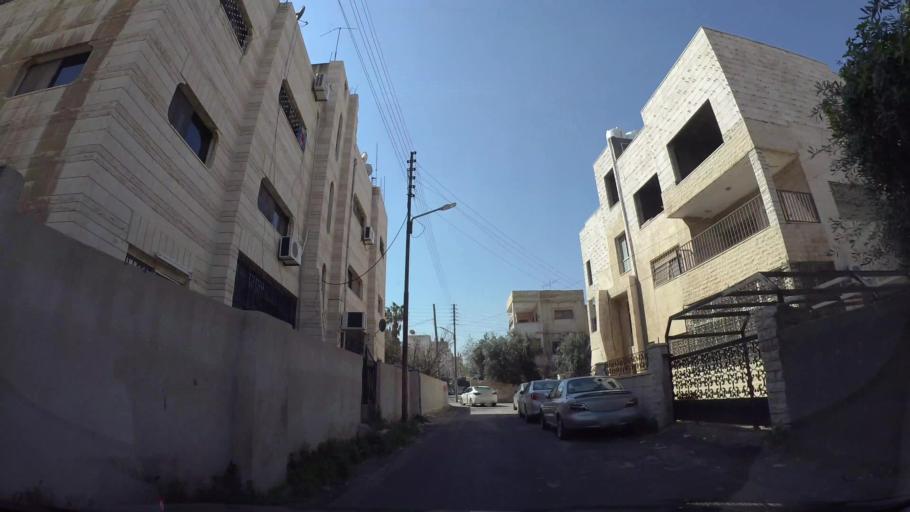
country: JO
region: Amman
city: Amman
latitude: 31.9870
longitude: 35.9804
